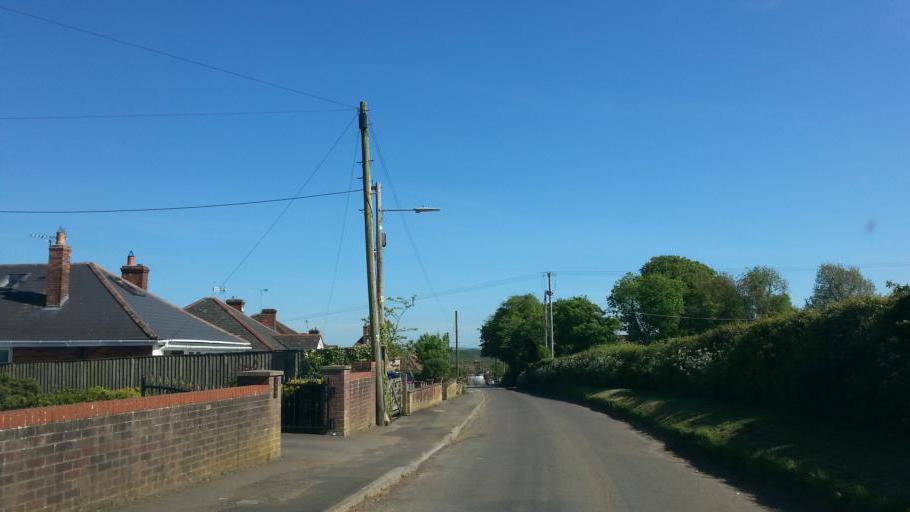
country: GB
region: England
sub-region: Somerset
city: Milborne Port
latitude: 50.9702
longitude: -2.4730
